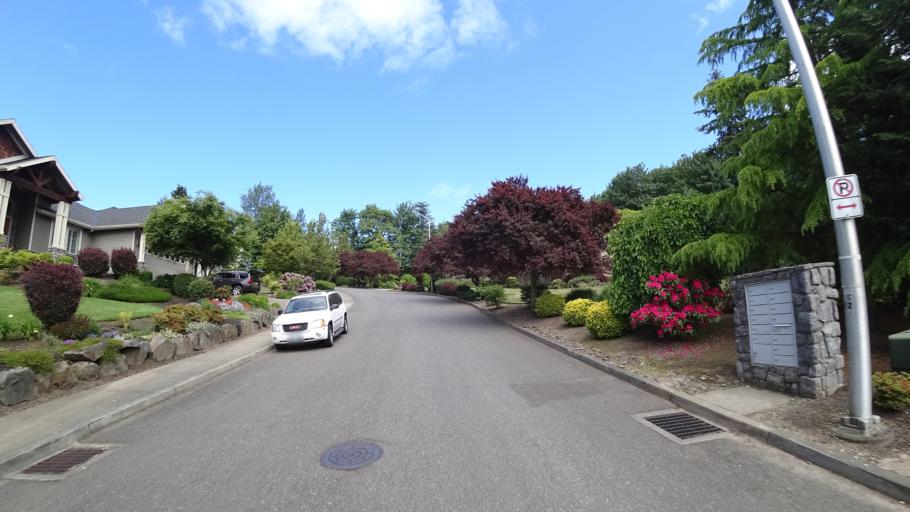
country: US
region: Oregon
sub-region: Washington County
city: Bethany
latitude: 45.5924
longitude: -122.8275
